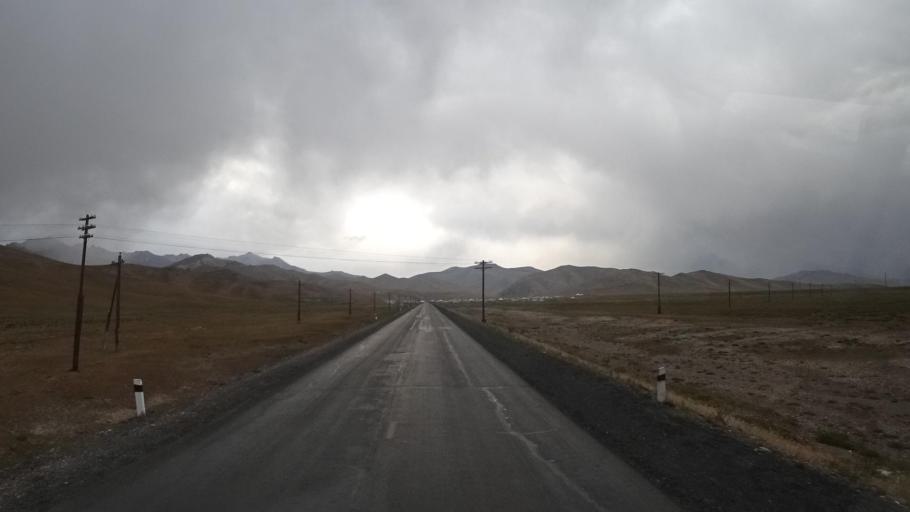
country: KG
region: Osh
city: Gul'cha
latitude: 39.7140
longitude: 73.2383
